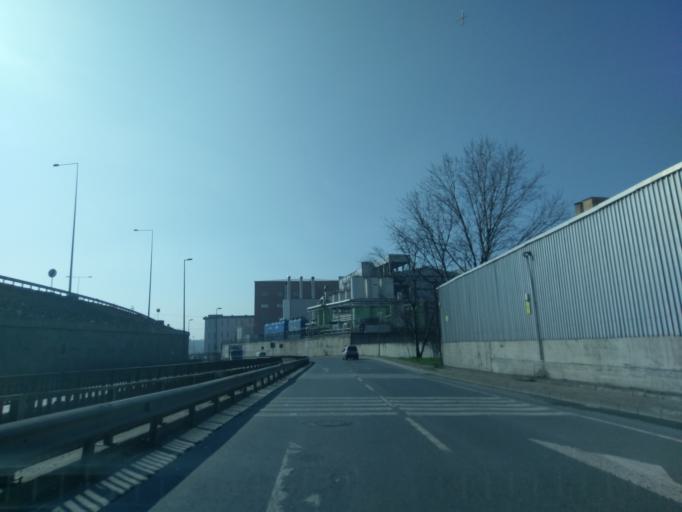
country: TR
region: Istanbul
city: Basaksehir
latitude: 41.0750
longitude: 28.8139
